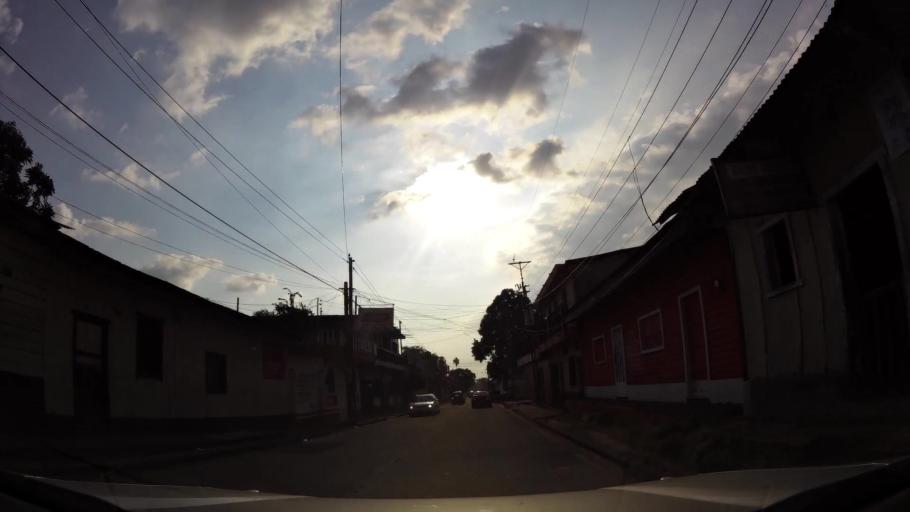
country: GT
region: Retalhuleu
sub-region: Municipio de Retalhuleu
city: Retalhuleu
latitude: 14.5420
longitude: -91.6785
